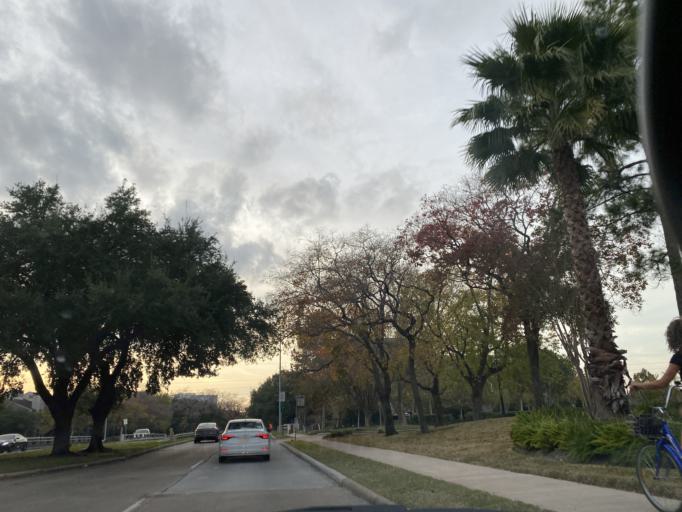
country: US
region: Texas
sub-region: Harris County
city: Bunker Hill Village
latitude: 29.7278
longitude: -95.5646
